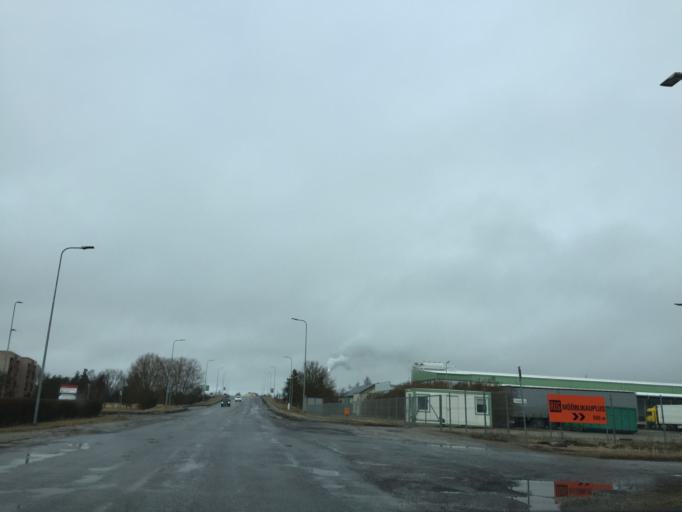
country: EE
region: Laeaene
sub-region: Haapsalu linn
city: Haapsalu
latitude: 58.9278
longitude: 23.5446
